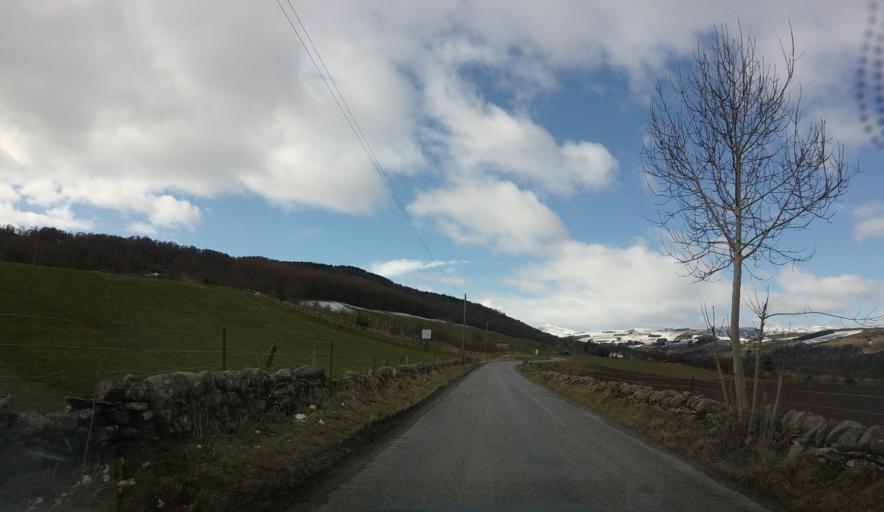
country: GB
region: Scotland
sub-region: Perth and Kinross
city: Pitlochry
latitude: 56.6472
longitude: -3.7234
